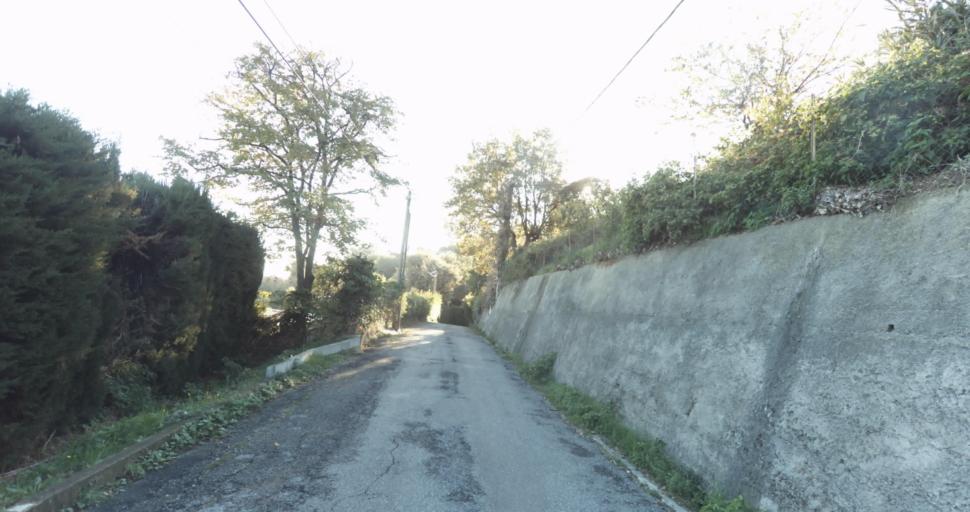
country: FR
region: Provence-Alpes-Cote d'Azur
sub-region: Departement des Alpes-Maritimes
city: Vence
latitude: 43.7328
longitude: 7.1192
